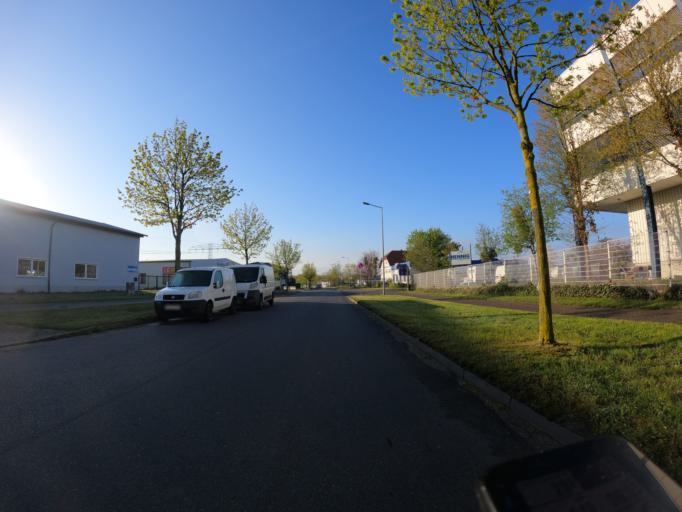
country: DE
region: Brandenburg
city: Neuenhagen
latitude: 52.5338
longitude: 13.7119
